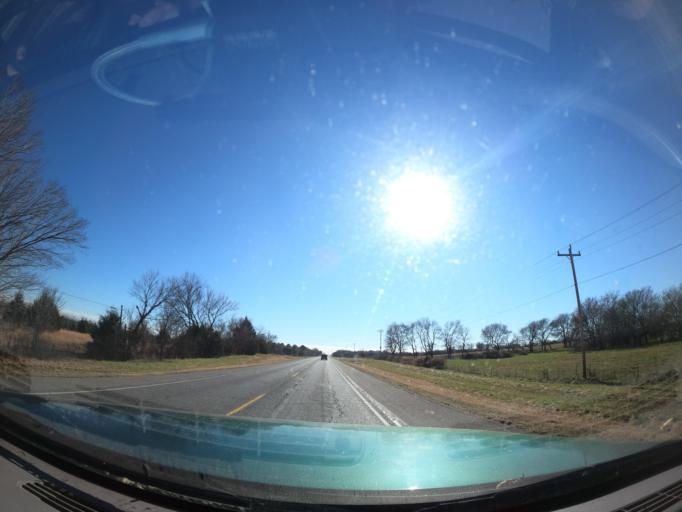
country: US
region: Oklahoma
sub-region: Muskogee County
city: Haskell
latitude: 35.8502
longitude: -95.6775
